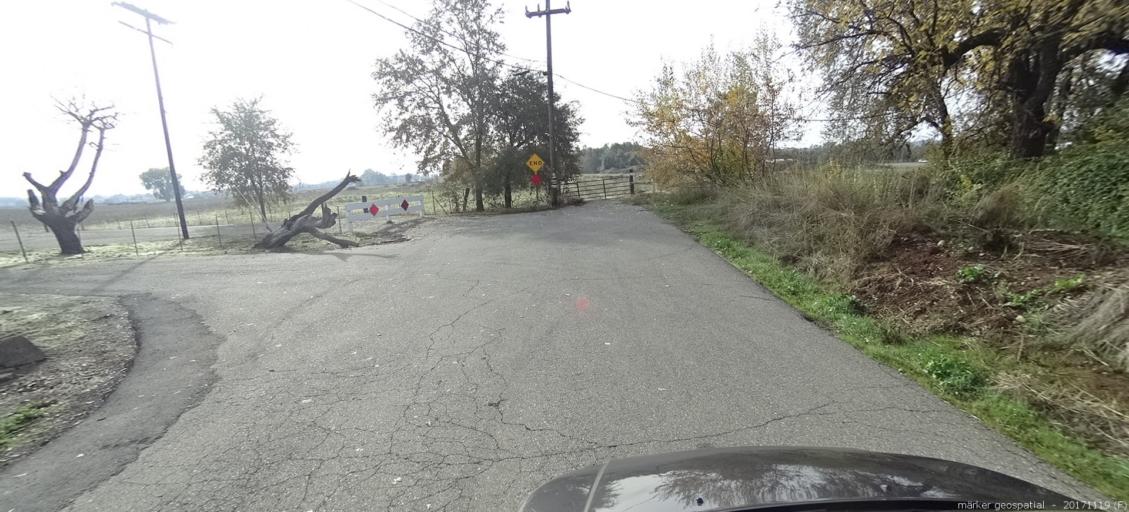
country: US
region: California
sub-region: Shasta County
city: Anderson
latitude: 40.5022
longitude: -122.3331
